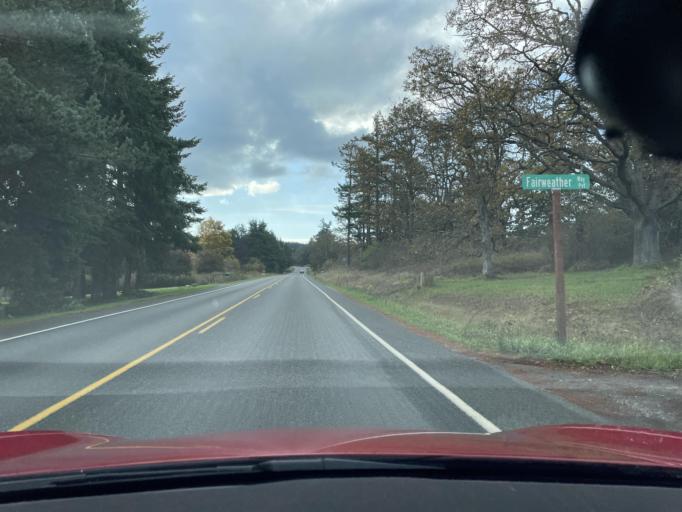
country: US
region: Washington
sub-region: San Juan County
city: Friday Harbor
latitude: 48.5075
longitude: -123.0362
